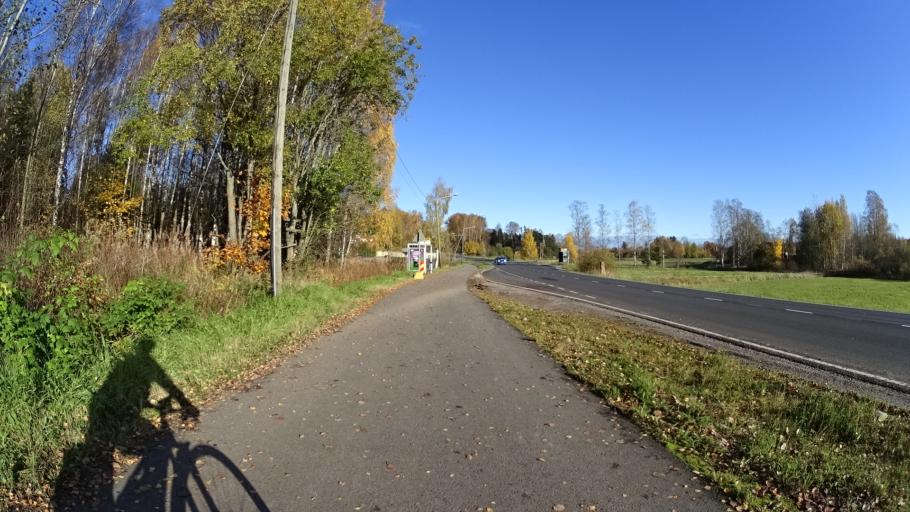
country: FI
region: Uusimaa
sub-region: Helsinki
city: Teekkarikylae
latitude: 60.2993
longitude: 24.8584
